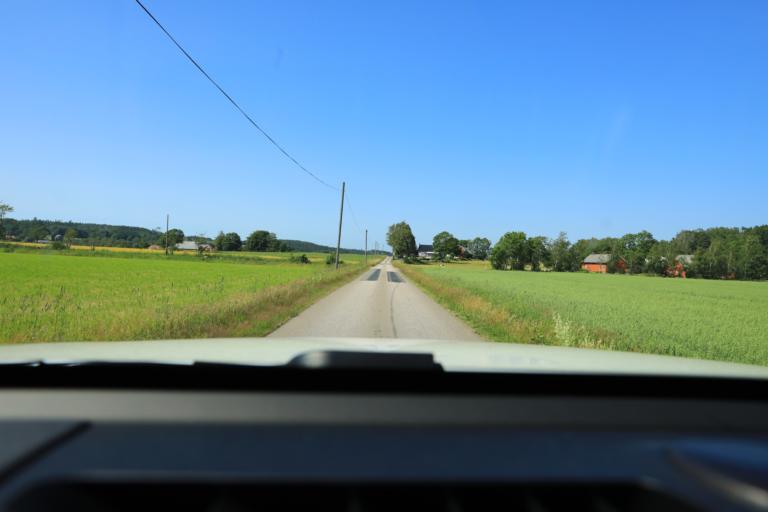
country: SE
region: Halland
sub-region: Varbergs Kommun
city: Veddige
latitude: 57.2033
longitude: 12.3187
